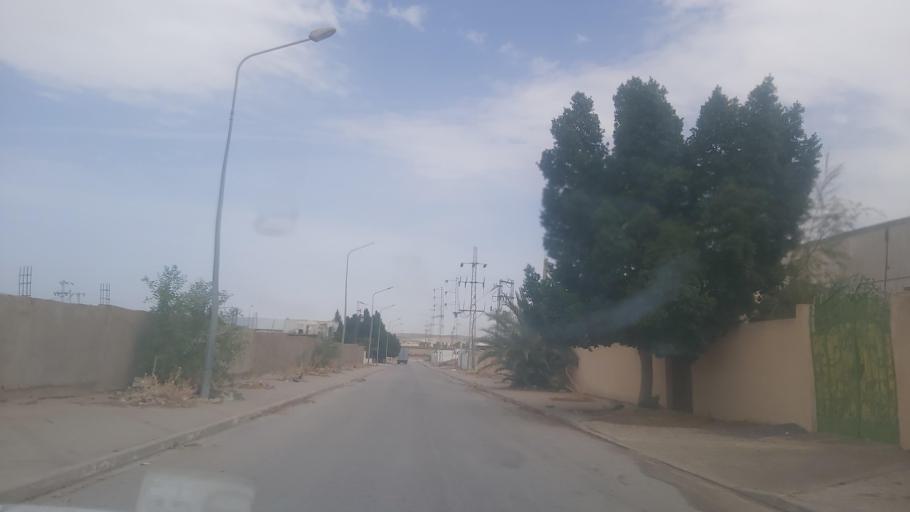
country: TN
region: Silyanah
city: Bu `Aradah
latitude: 36.3512
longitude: 9.6345
